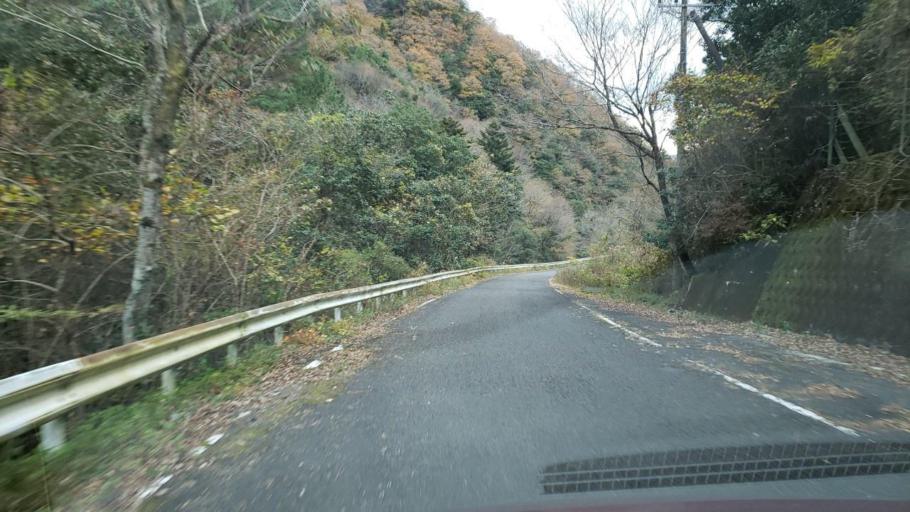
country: JP
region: Tokushima
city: Wakimachi
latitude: 34.1345
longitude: 134.2301
